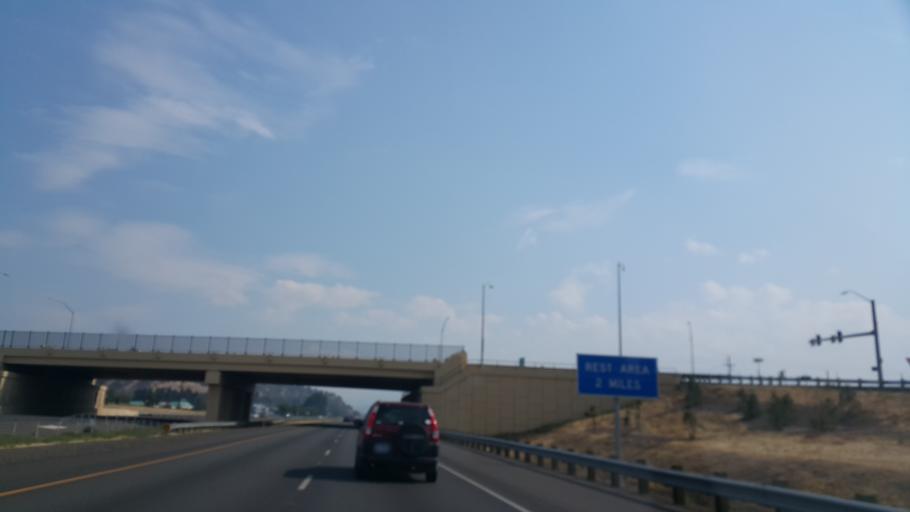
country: US
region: Oregon
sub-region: Jackson County
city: Phoenix
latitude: 42.2819
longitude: -122.8160
